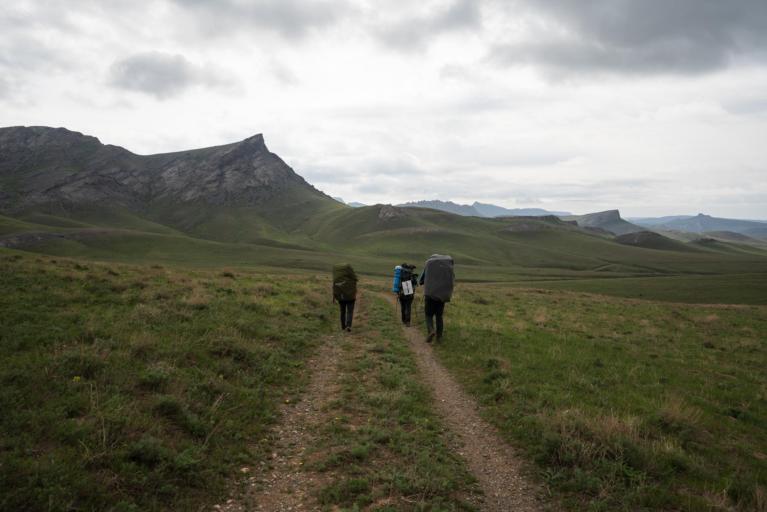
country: KZ
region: Ongtustik Qazaqstan
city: Ashchysay
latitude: 43.5924
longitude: 68.9110
